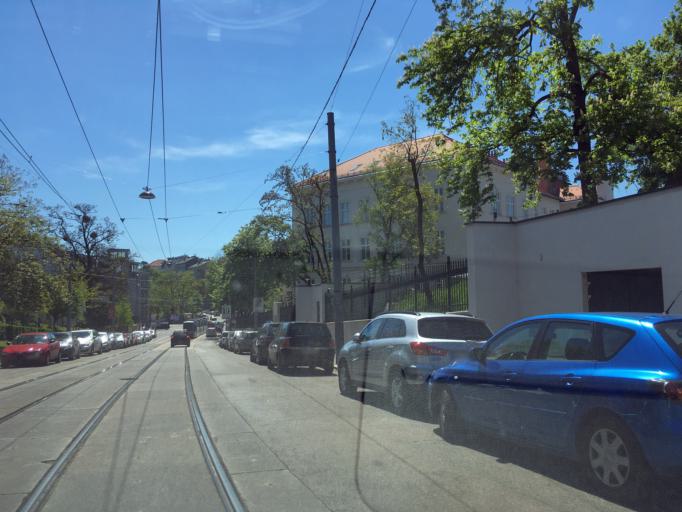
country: AT
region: Vienna
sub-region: Wien Stadt
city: Vienna
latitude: 48.2459
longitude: 16.3561
